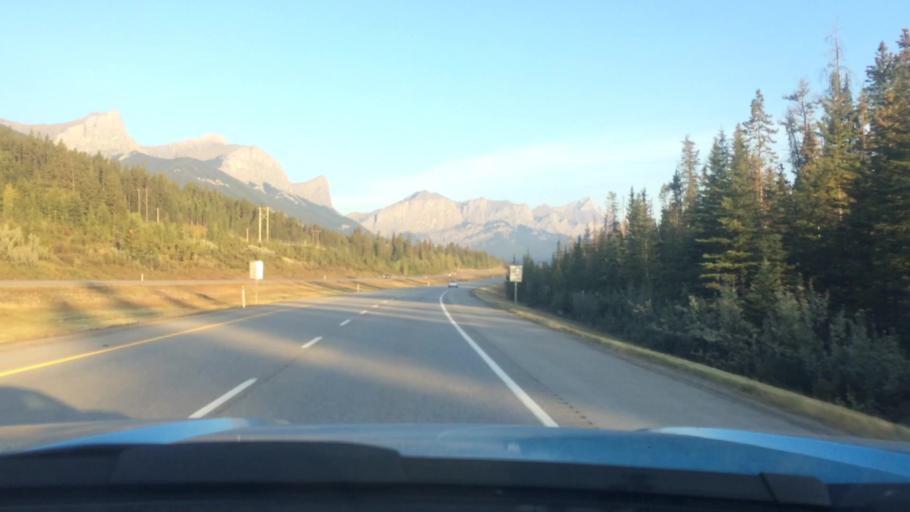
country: CA
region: Alberta
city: Canmore
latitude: 51.0408
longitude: -115.2789
